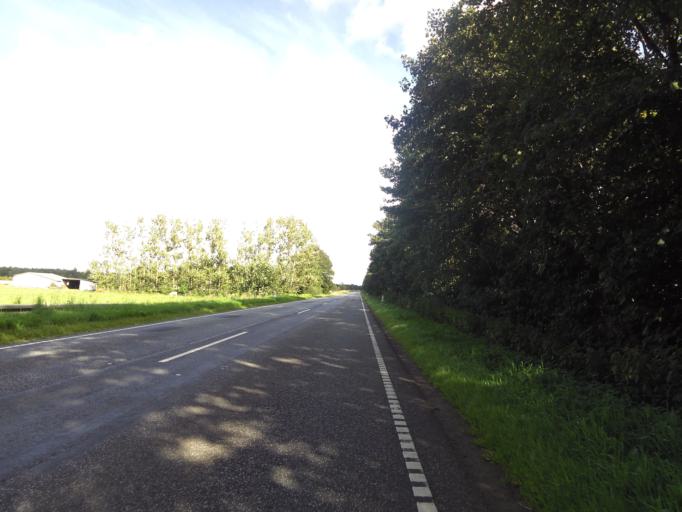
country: DK
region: South Denmark
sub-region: Tonder Kommune
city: Toftlund
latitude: 55.2181
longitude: 9.0223
